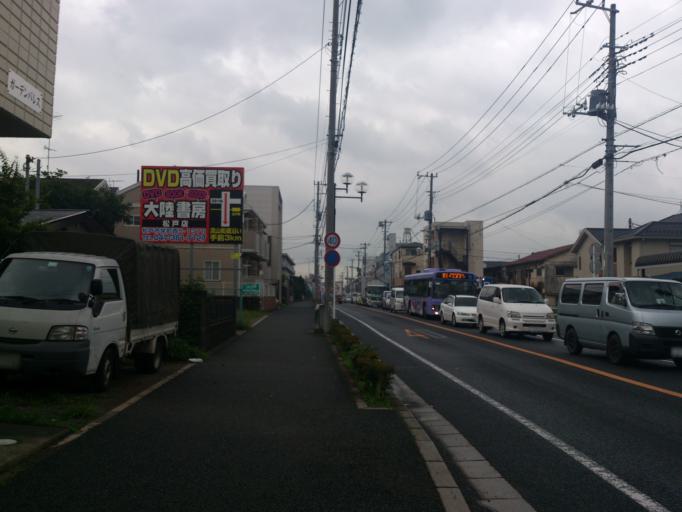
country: JP
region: Chiba
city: Matsudo
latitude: 35.7842
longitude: 139.9103
